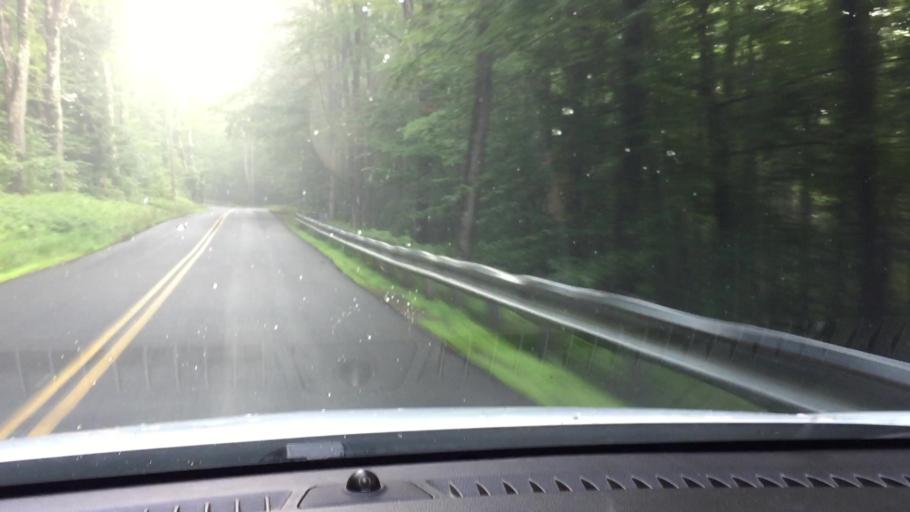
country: US
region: Massachusetts
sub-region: Berkshire County
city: Becket
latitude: 42.4158
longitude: -72.9825
